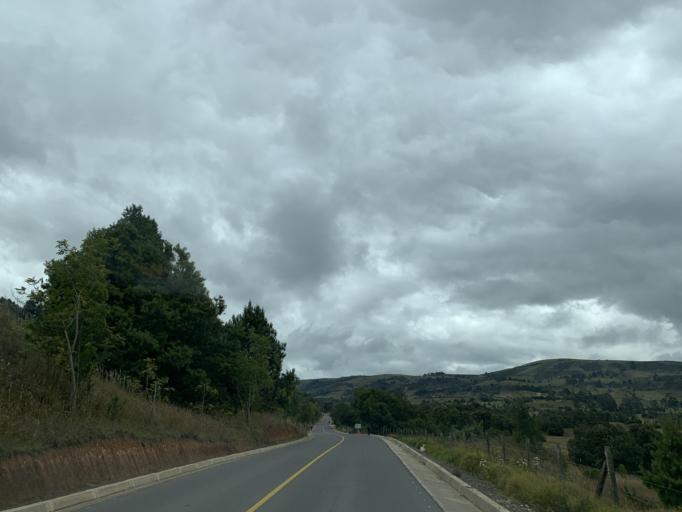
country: CO
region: Boyaca
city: Tunja
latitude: 5.5280
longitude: -73.3210
